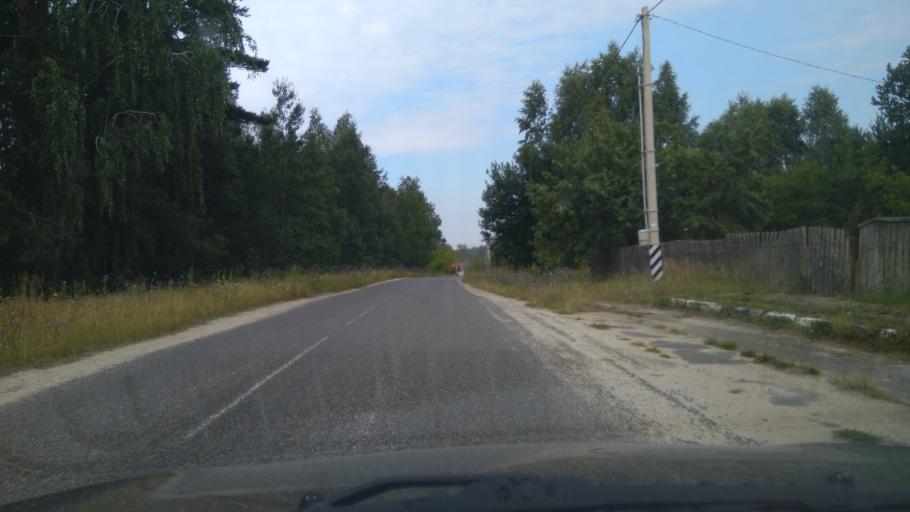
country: BY
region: Brest
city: Nyakhachava
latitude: 52.6090
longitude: 25.0914
